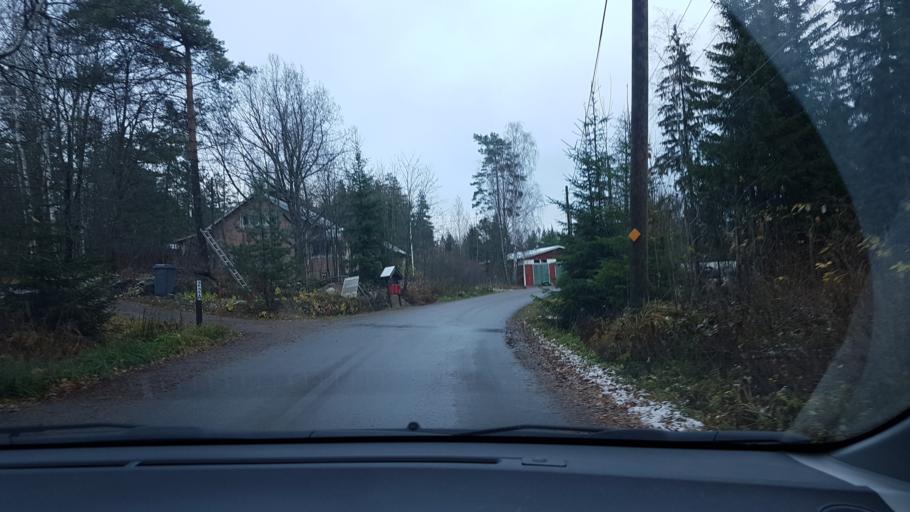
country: FI
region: Uusimaa
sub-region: Helsinki
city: Vantaa
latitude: 60.2819
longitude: 25.1559
